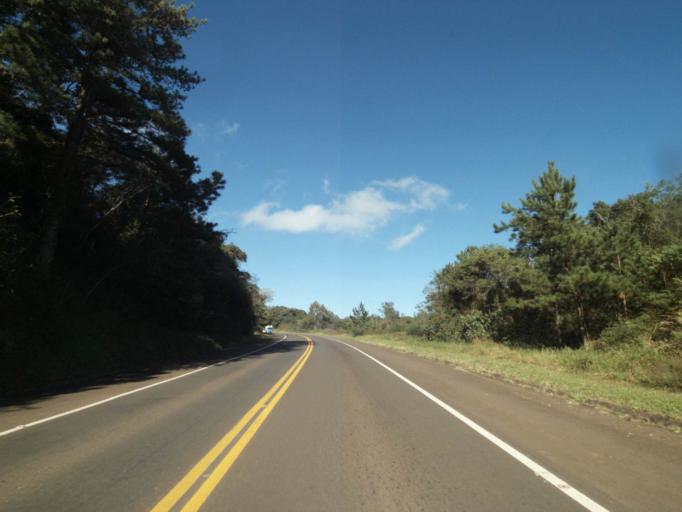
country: BR
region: Parana
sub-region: Faxinal
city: Faxinal
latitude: -23.8930
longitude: -51.1873
